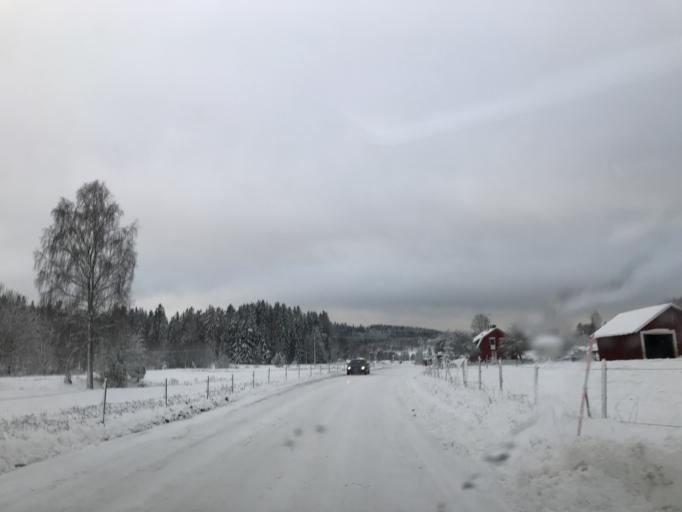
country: SE
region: Vaestra Goetaland
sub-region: Svenljunga Kommun
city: Svenljunga
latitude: 57.3946
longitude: 13.0718
